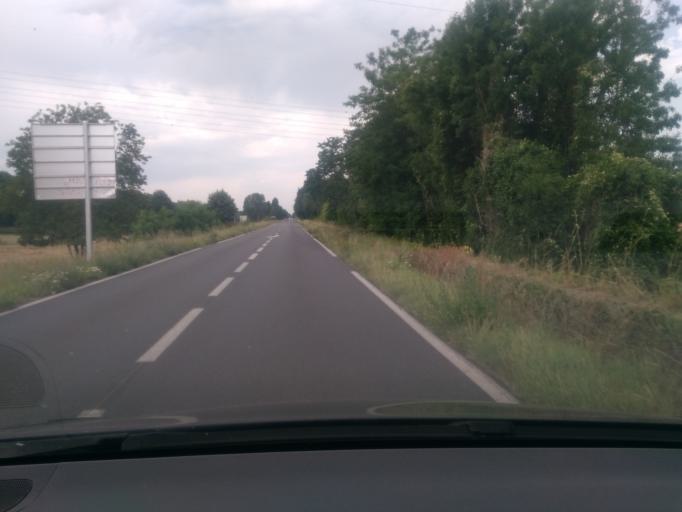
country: FR
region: Pays de la Loire
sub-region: Departement de Maine-et-Loire
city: Varennes-sur-Loire
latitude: 47.2213
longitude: 0.0424
